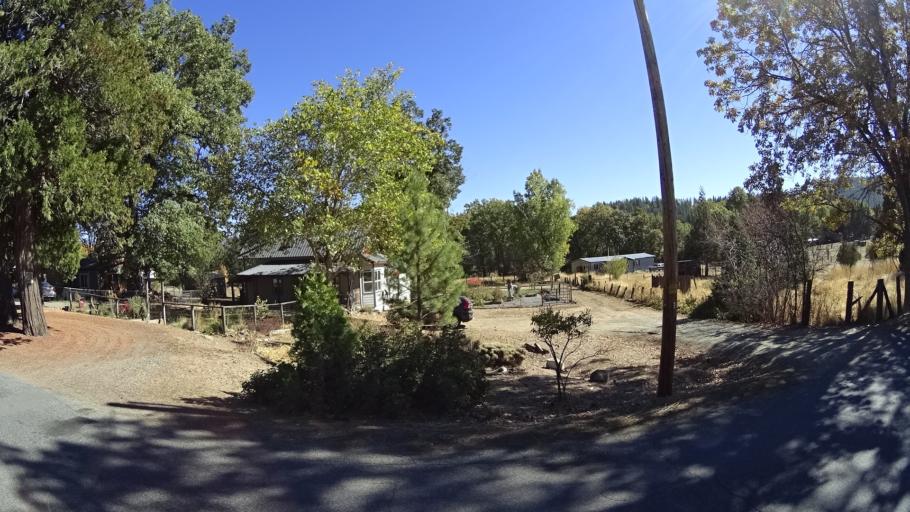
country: US
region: California
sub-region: Siskiyou County
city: Yreka
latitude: 41.4519
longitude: -122.8986
